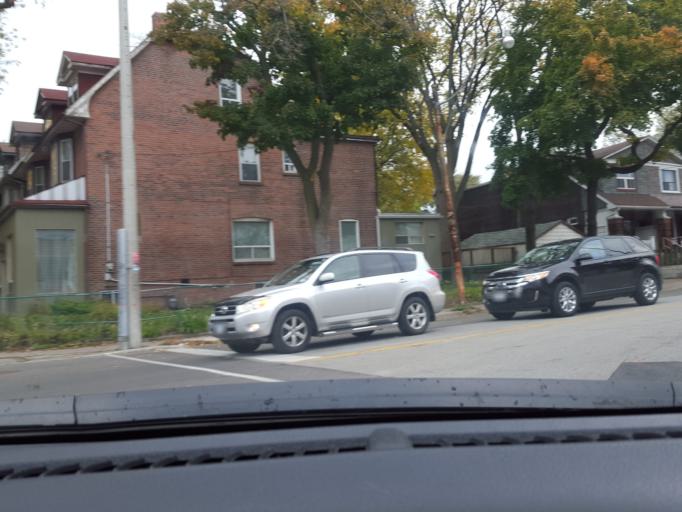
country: CA
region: Ontario
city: Toronto
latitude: 43.6707
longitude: -79.3439
